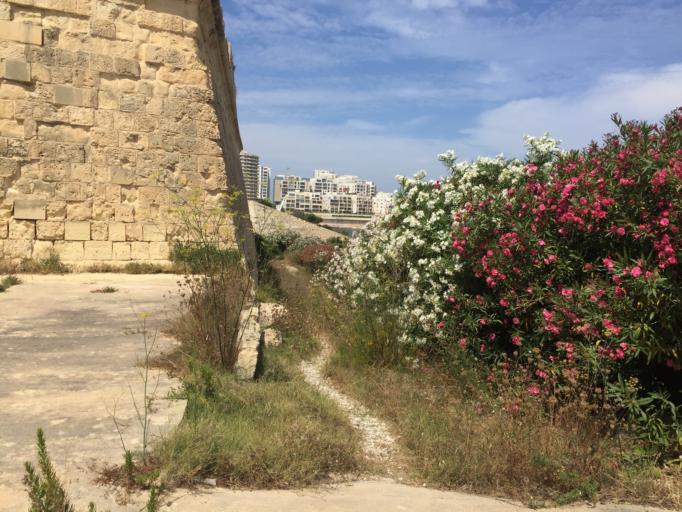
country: MT
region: Il-Furjana
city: Floriana
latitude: 35.9028
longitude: 14.5060
